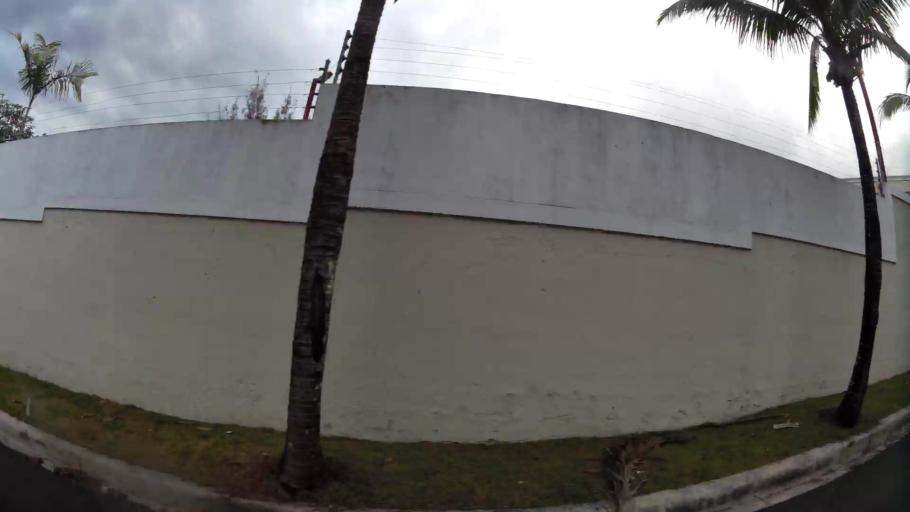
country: DO
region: Nacional
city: Santo Domingo
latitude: 18.5150
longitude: -69.9634
